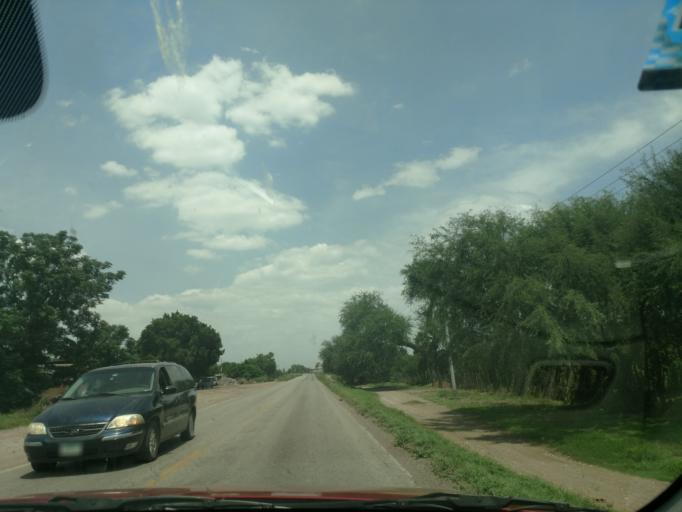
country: MX
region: San Luis Potosi
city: Ciudad Fernandez
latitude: 21.9528
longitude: -100.0670
